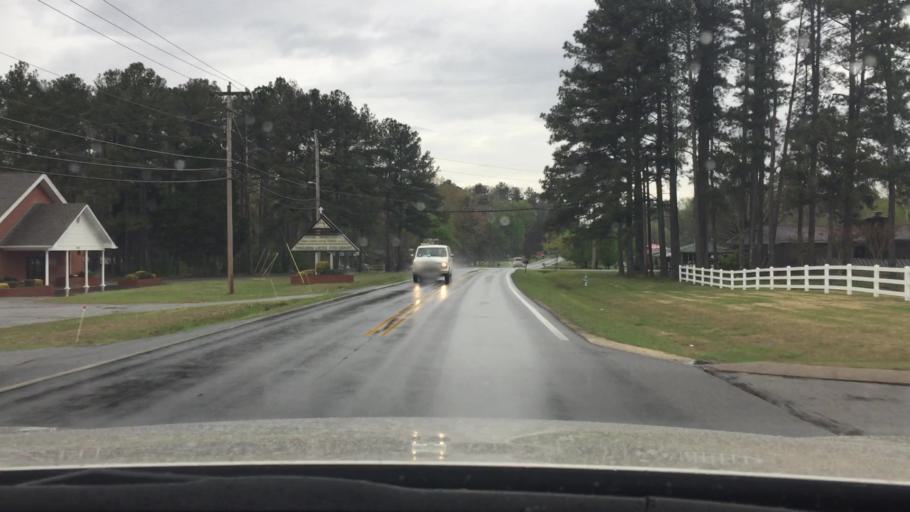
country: US
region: Georgia
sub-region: Catoosa County
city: Lakeview
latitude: 34.9697
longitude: -85.2357
